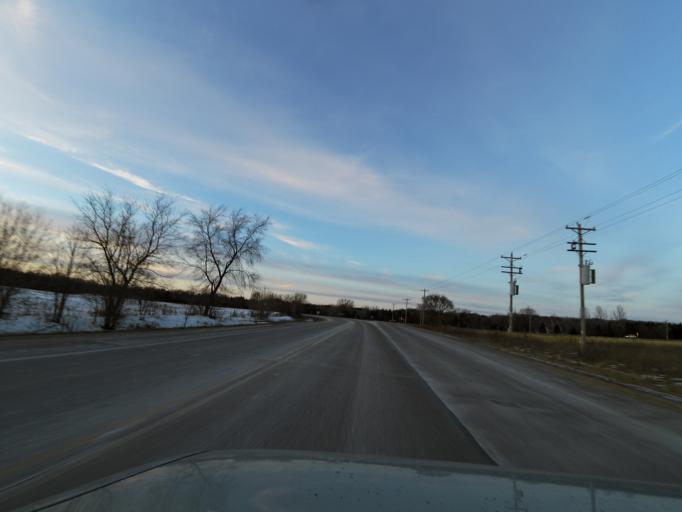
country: US
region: Minnesota
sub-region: Washington County
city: Bayport
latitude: 45.0263
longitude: -92.7469
